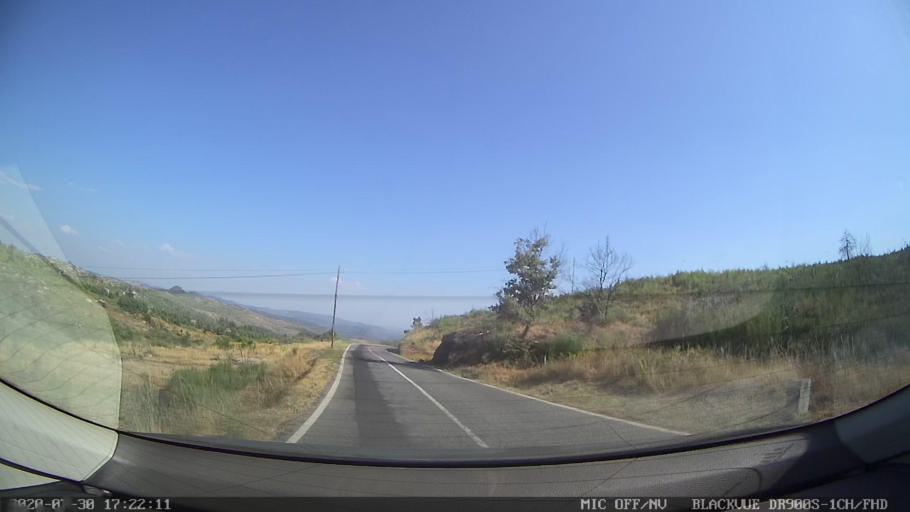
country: PT
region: Vila Real
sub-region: Murca
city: Murca
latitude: 41.3029
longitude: -7.4768
